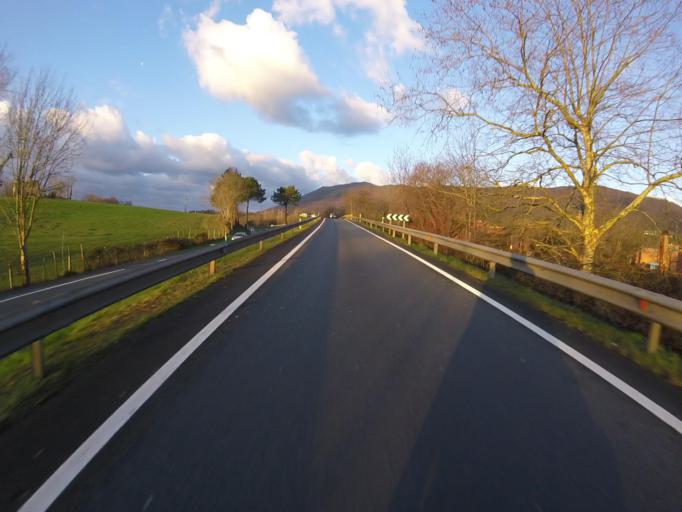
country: ES
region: Basque Country
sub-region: Provincia de Guipuzcoa
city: Irun
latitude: 43.3476
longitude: -1.8106
